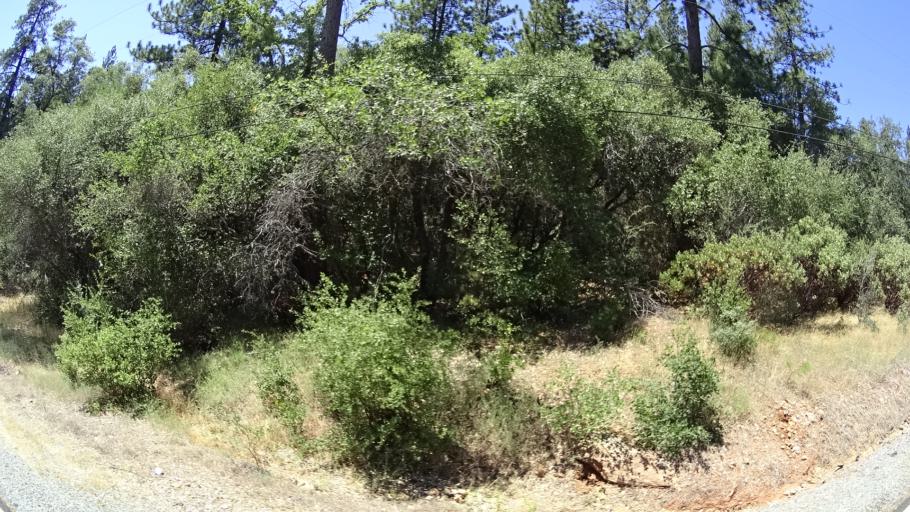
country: US
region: California
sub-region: Calaveras County
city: Murphys
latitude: 38.1371
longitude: -120.4964
